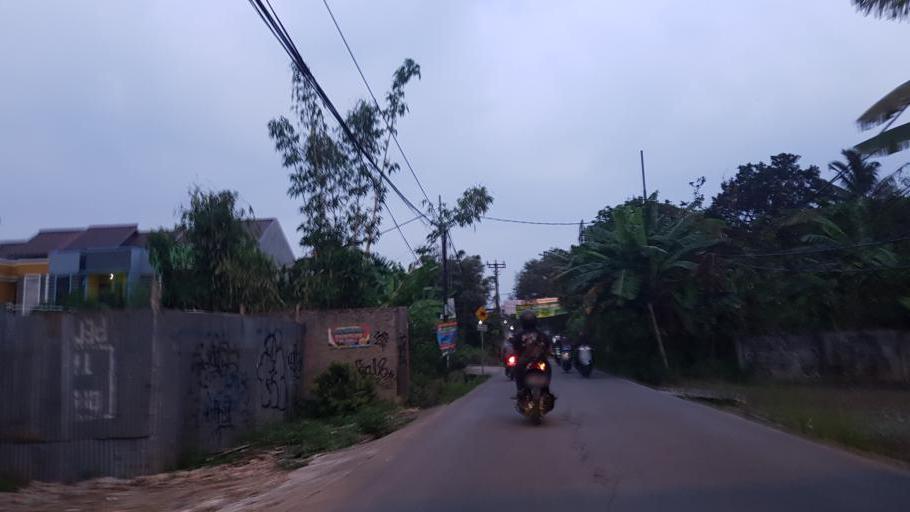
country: ID
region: West Java
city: Depok
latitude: -6.3689
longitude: 106.7998
